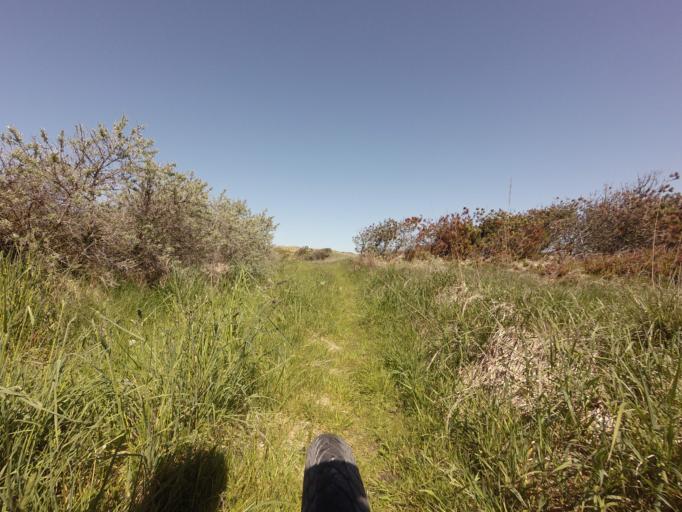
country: DK
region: North Denmark
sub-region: Jammerbugt Kommune
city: Pandrup
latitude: 57.2328
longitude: 9.5581
